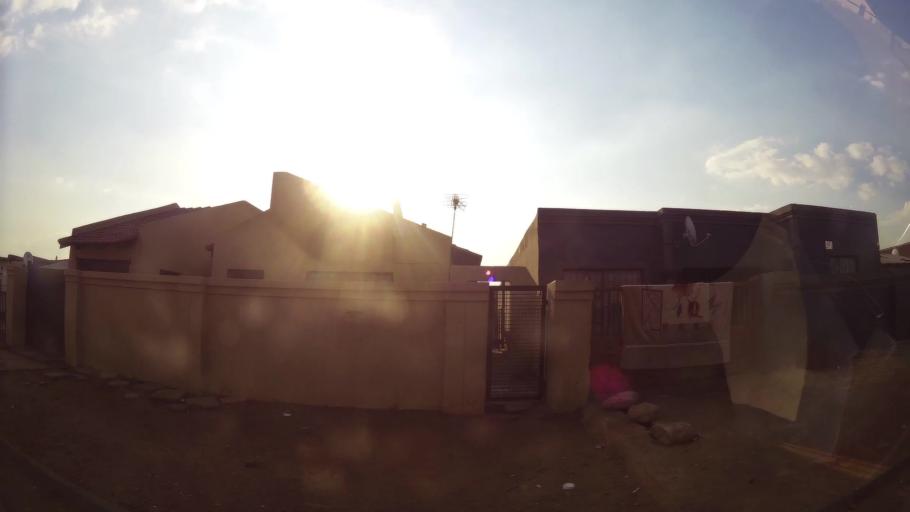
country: ZA
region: Gauteng
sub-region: Ekurhuleni Metropolitan Municipality
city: Germiston
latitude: -26.3529
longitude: 28.2065
